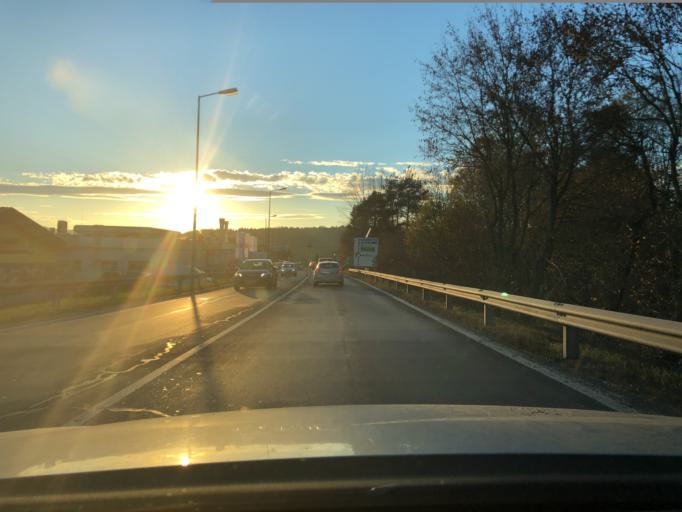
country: AT
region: Styria
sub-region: Politischer Bezirk Weiz
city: Gleisdorf
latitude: 47.1125
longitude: 15.7077
